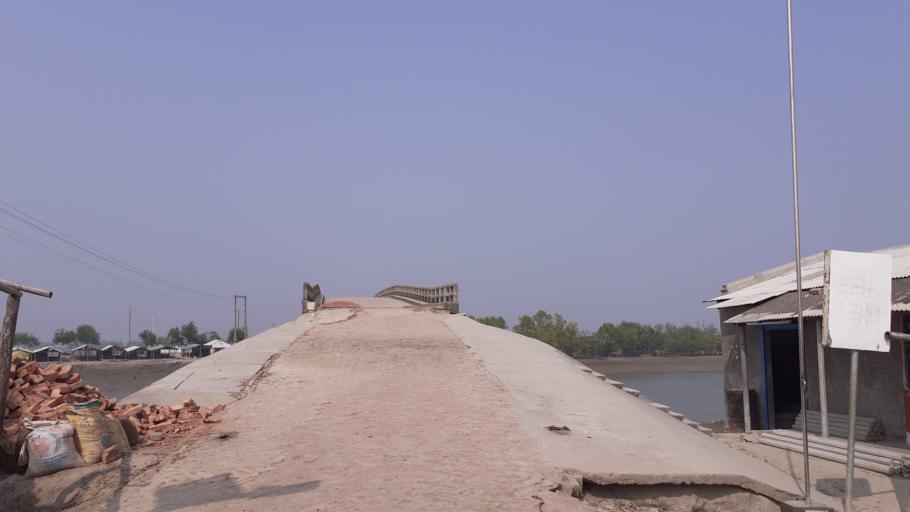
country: IN
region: West Bengal
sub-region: North 24 Parganas
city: Taki
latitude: 22.2879
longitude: 89.2740
